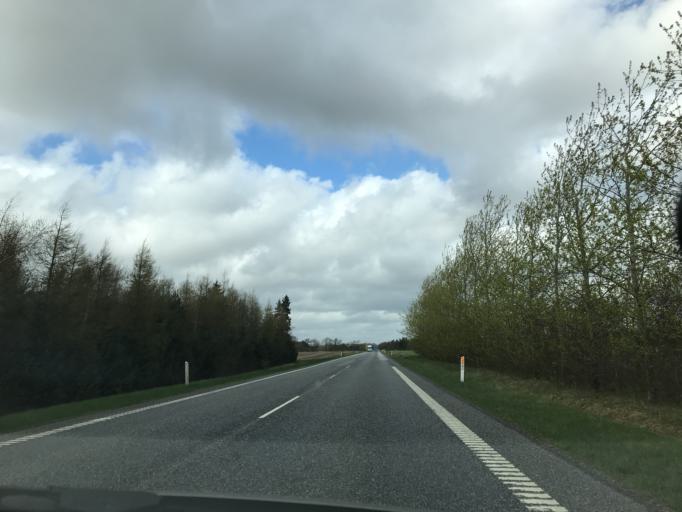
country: DK
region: Central Jutland
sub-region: Viborg Kommune
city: Stoholm
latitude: 56.3947
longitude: 8.9981
